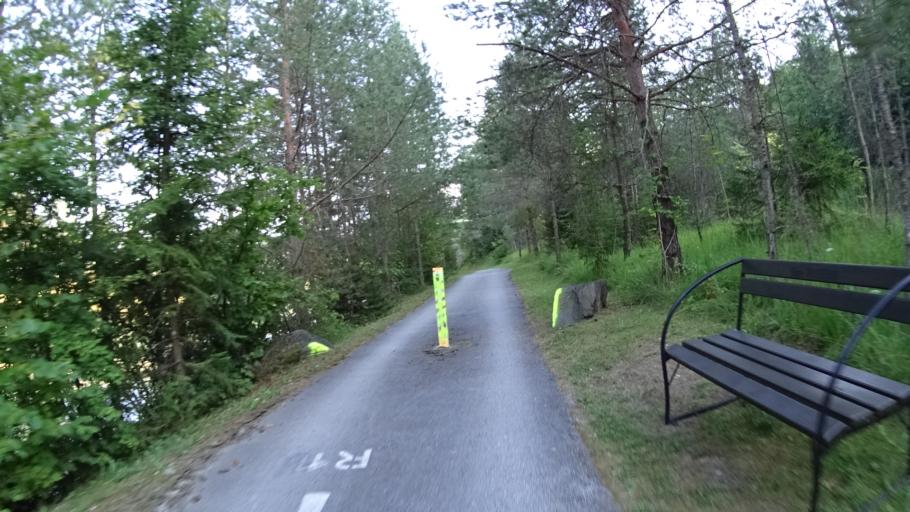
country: AT
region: Carinthia
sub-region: Politischer Bezirk Villach Land
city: Rosegg
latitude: 46.5753
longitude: 14.0209
